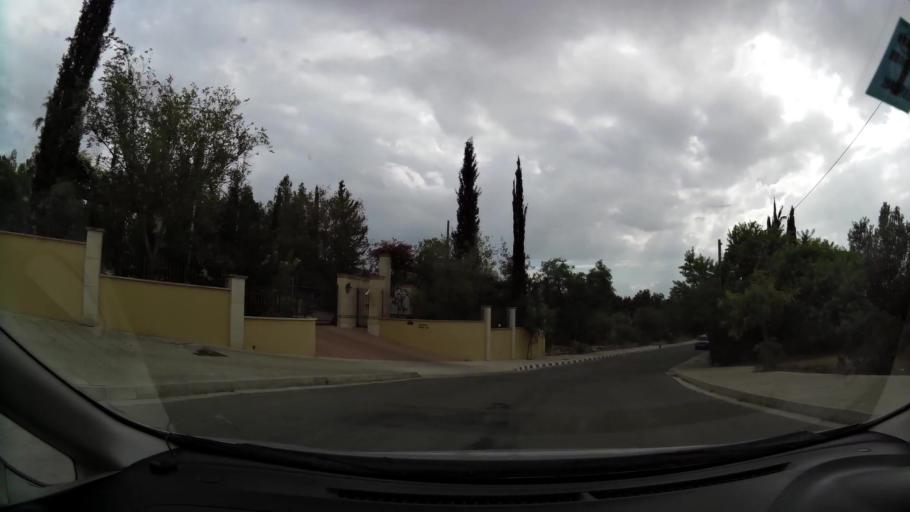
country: CY
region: Lefkosia
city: Geri
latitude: 35.1208
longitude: 33.3868
